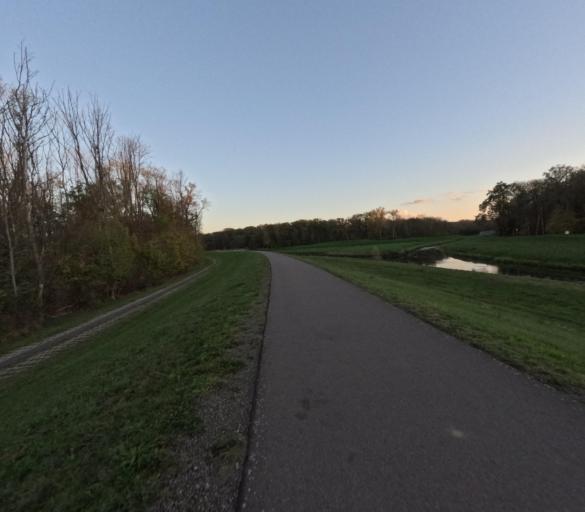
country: DE
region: Saxony
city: Leipzig
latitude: 51.3690
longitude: 12.3104
